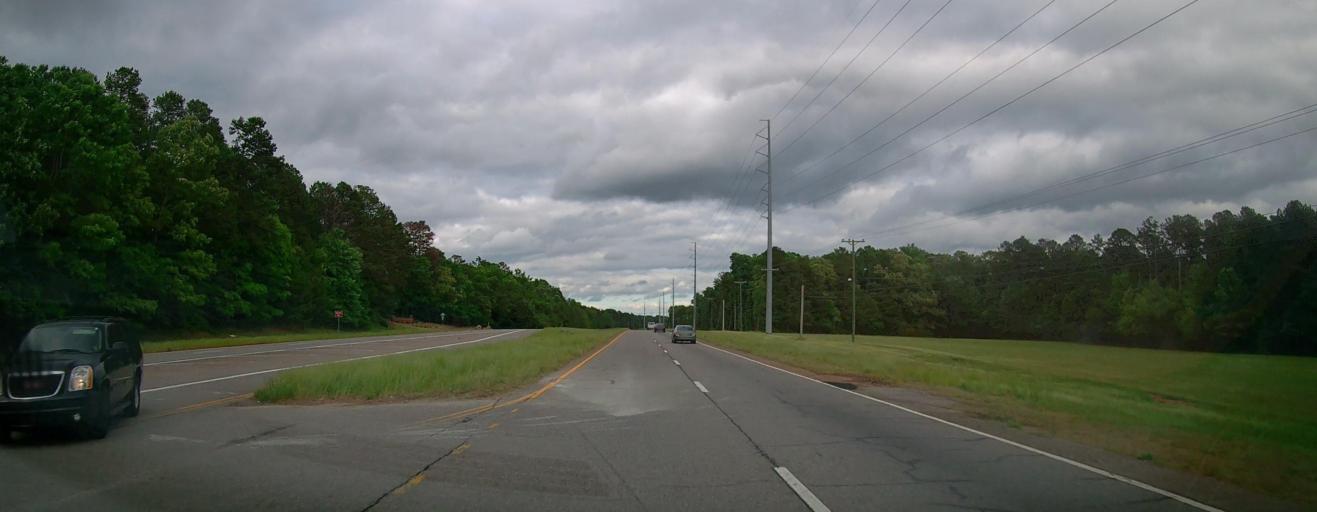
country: US
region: Georgia
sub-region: Oconee County
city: Bogart
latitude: 33.9181
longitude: -83.5449
